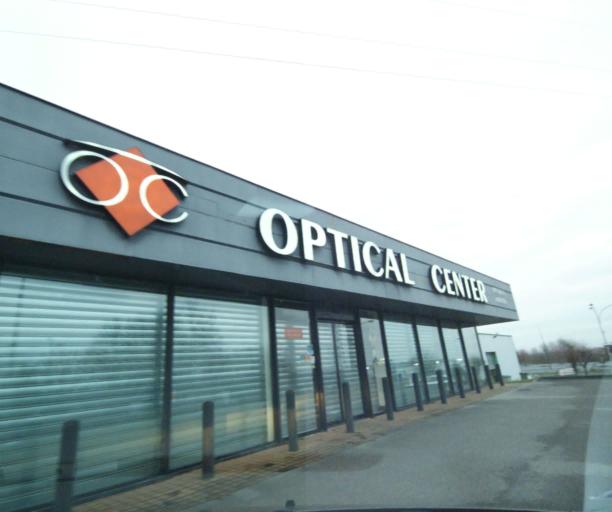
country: FR
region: Picardie
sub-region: Departement de l'Oise
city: Noyon
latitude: 49.5714
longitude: 2.9773
